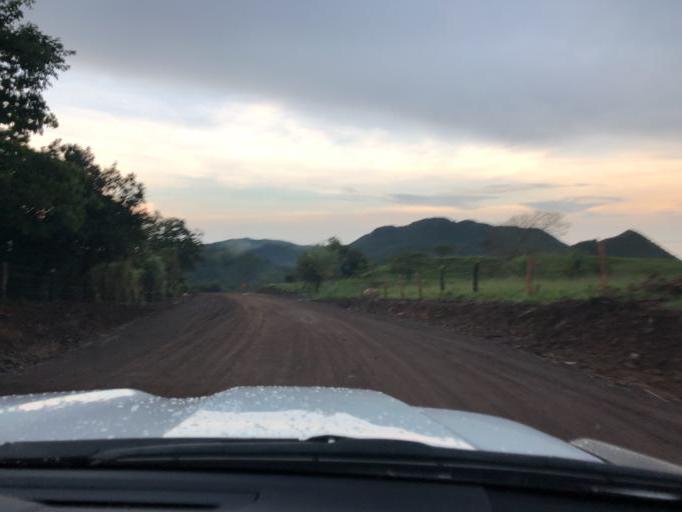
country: NI
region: Chontales
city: La Libertad
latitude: 12.1853
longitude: -85.1745
